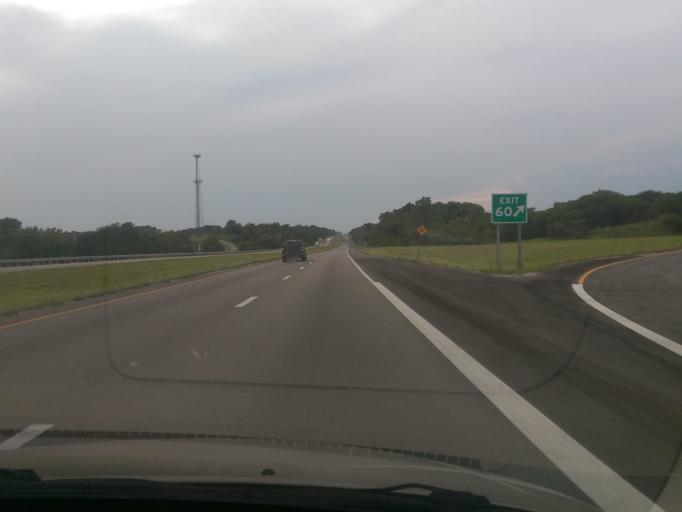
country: US
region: Missouri
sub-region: Andrew County
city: Savannah
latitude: 39.9176
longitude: -94.9065
